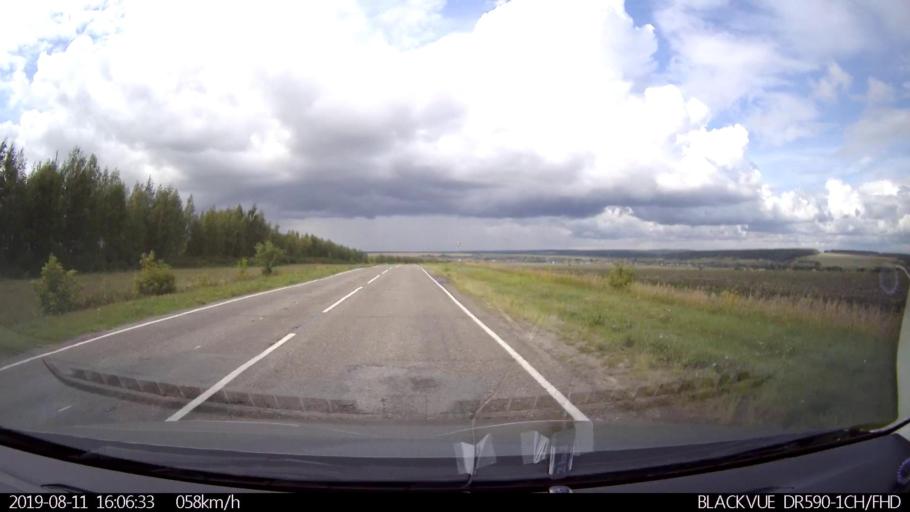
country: RU
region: Ulyanovsk
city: Ignatovka
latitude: 53.9700
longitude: 47.6482
